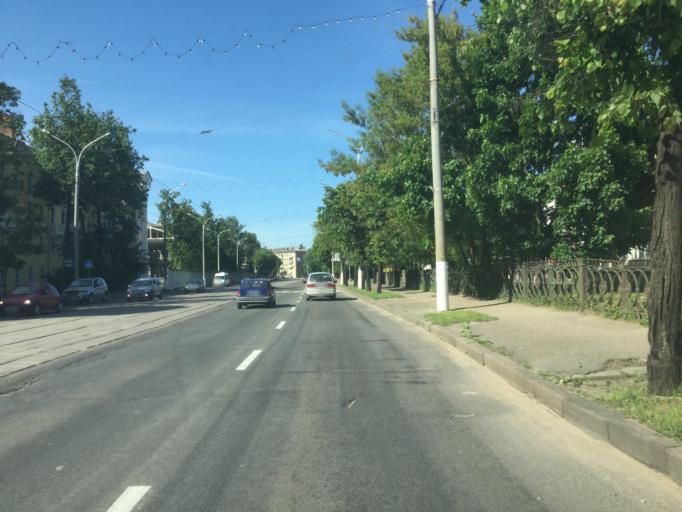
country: BY
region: Vitebsk
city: Vitebsk
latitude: 55.1884
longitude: 30.1895
